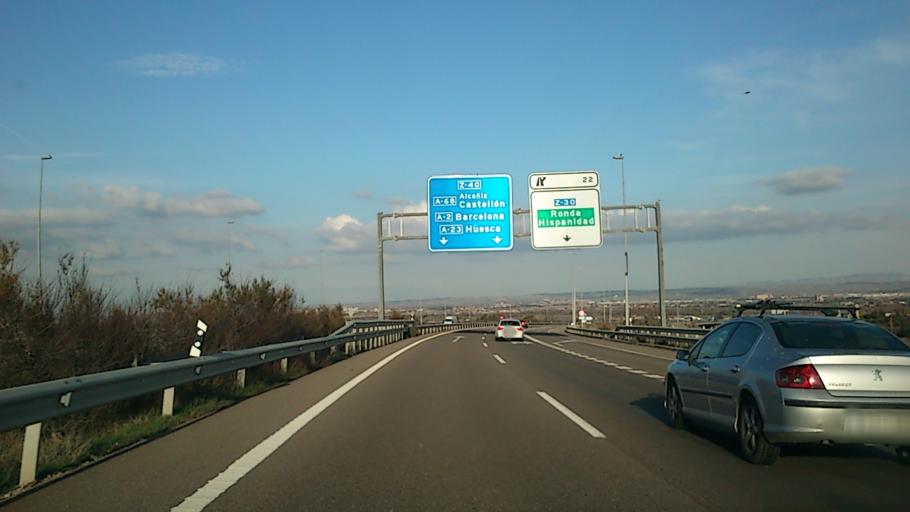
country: ES
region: Aragon
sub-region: Provincia de Zaragoza
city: Zaragoza
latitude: 41.6177
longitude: -0.8675
